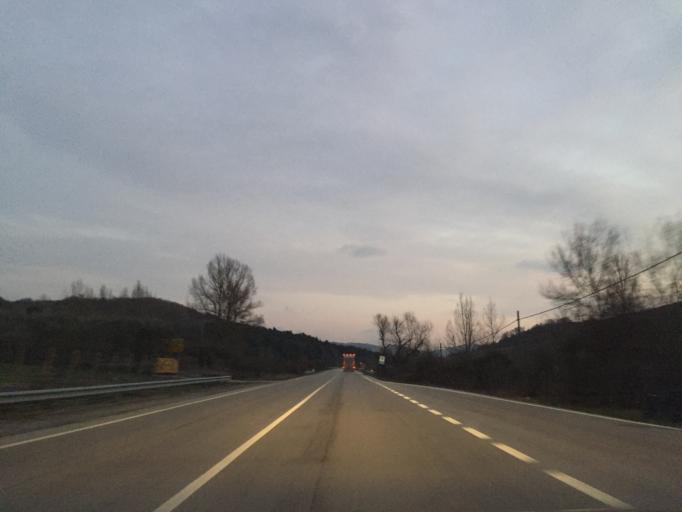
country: IT
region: Apulia
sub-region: Provincia di Foggia
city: Volturara Appula
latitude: 41.4845
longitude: 15.0516
